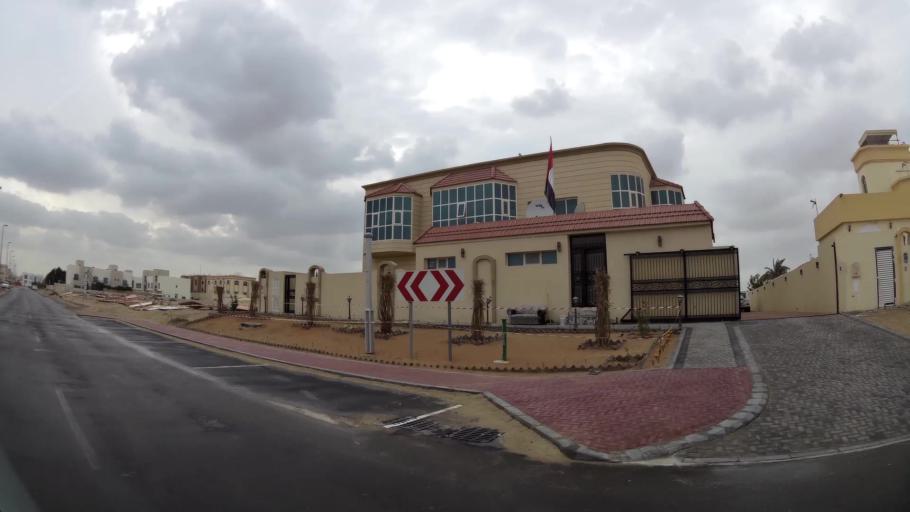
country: AE
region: Abu Dhabi
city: Abu Dhabi
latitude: 24.3503
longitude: 54.6324
